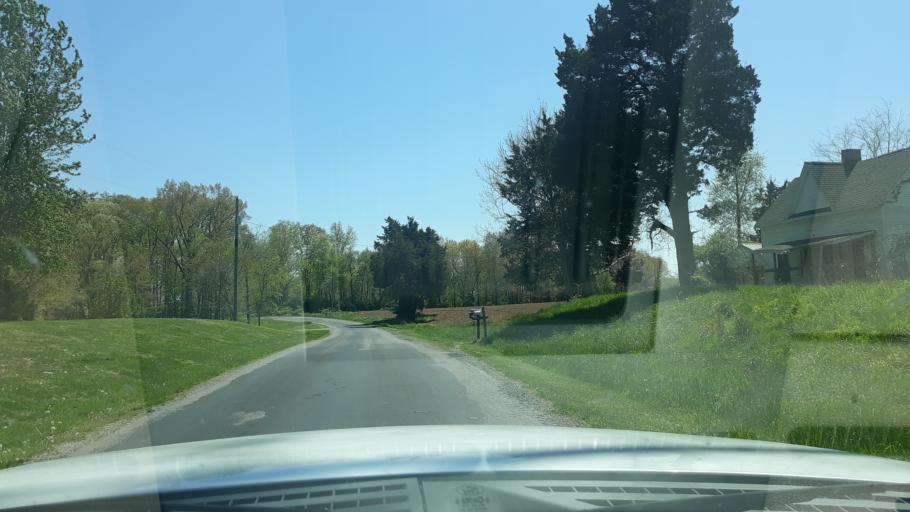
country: US
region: Illinois
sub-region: Saline County
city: Harrisburg
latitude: 37.8588
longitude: -88.6387
